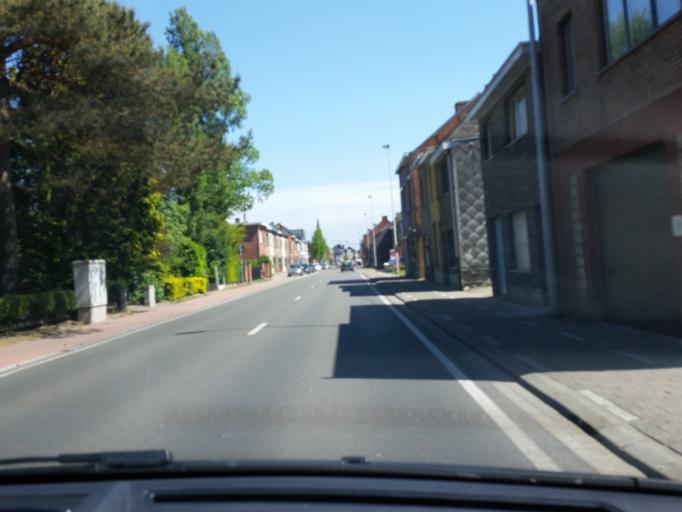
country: BE
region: Flanders
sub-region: Provincie Antwerpen
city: Bonheiden
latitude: 51.0252
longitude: 4.5390
